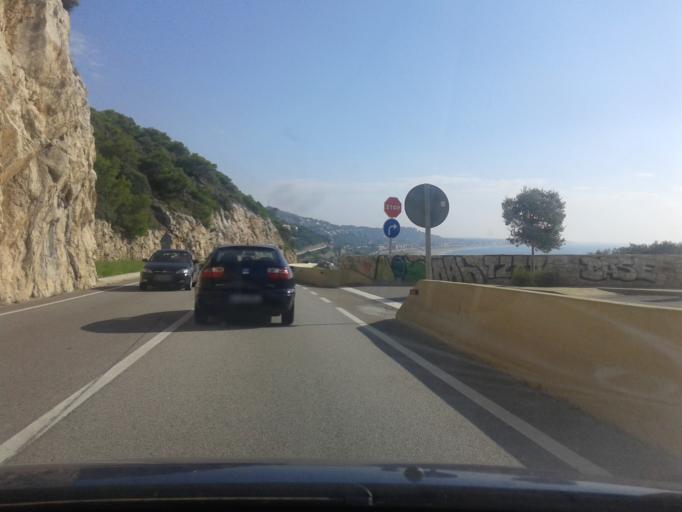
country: ES
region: Catalonia
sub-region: Provincia de Barcelona
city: Castelldefels
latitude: 41.2575
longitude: 1.9156
